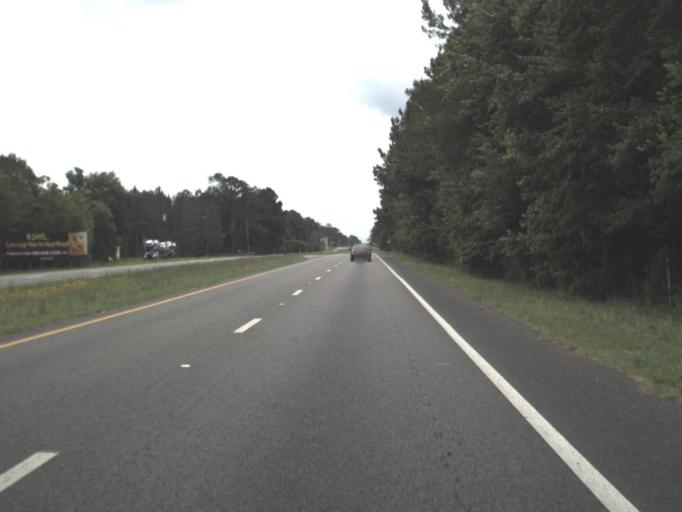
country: US
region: Florida
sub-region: Nassau County
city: Hilliard
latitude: 30.7144
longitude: -81.9341
